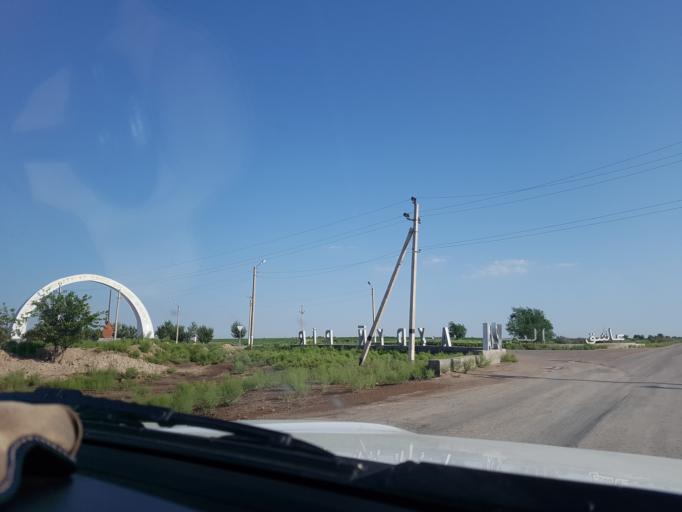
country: TM
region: Dasoguz
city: Koeneuergench
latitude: 41.8623
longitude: 58.7055
